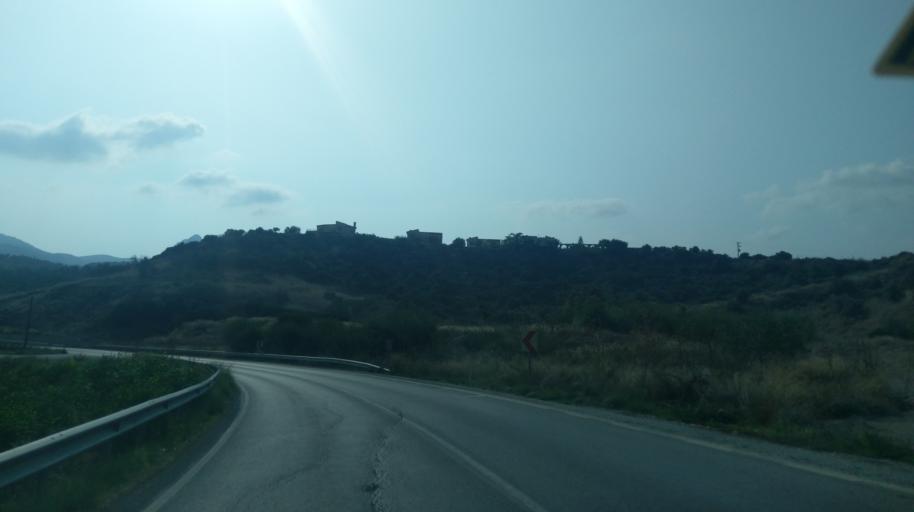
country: CY
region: Keryneia
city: Kyrenia
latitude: 35.3277
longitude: 33.4655
